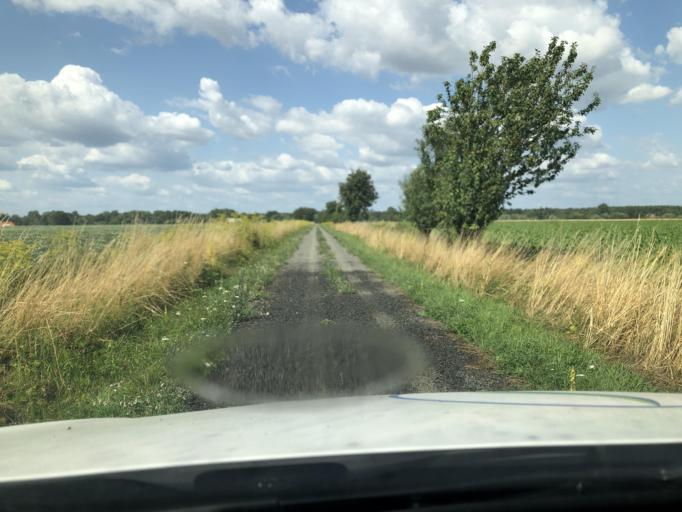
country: SE
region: Skane
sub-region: Kristianstads Kommun
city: Degeberga
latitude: 55.8915
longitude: 14.0803
